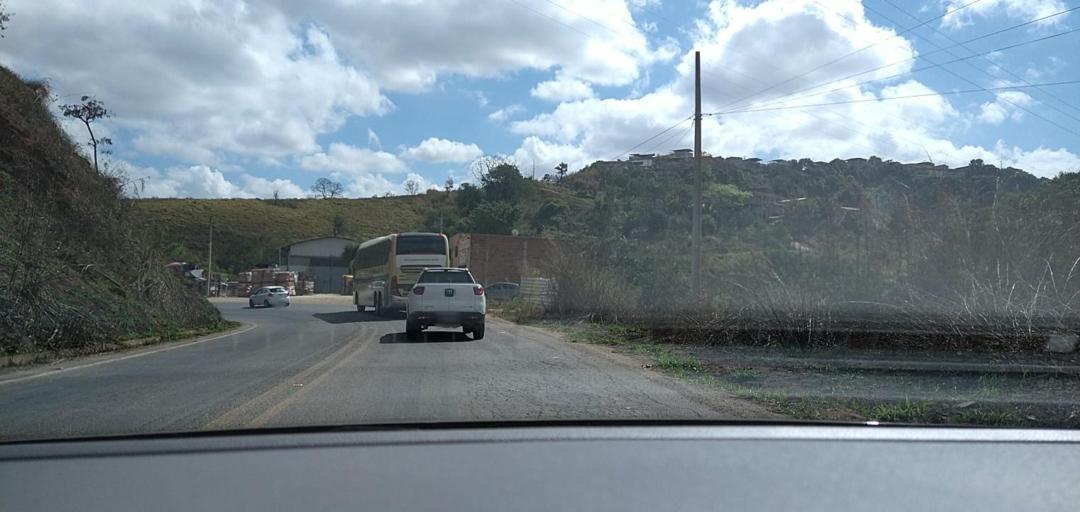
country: BR
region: Minas Gerais
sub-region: Ponte Nova
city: Ponte Nova
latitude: -20.4241
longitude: -42.8948
